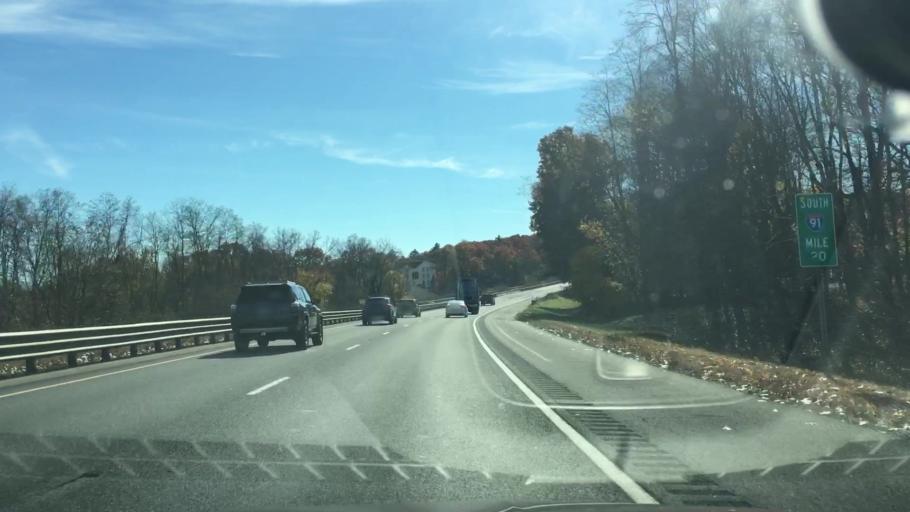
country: US
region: Massachusetts
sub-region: Hampshire County
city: South Hadley
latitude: 42.2759
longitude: -72.6059
